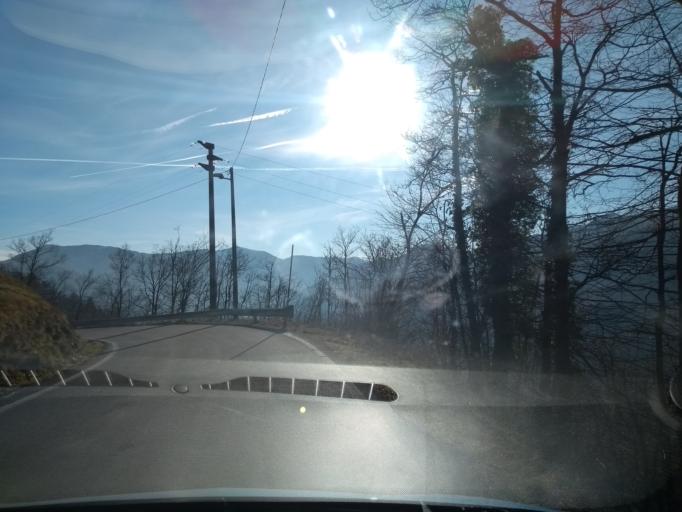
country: IT
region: Piedmont
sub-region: Provincia di Torino
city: Traves
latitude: 45.2820
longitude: 7.4373
